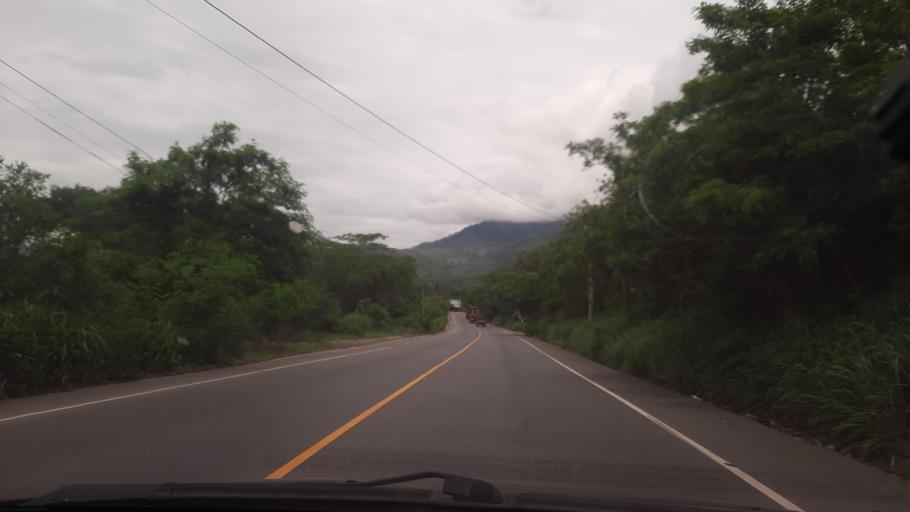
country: GT
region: Zacapa
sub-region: Municipio de Zacapa
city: Gualan
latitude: 15.1830
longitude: -89.2949
